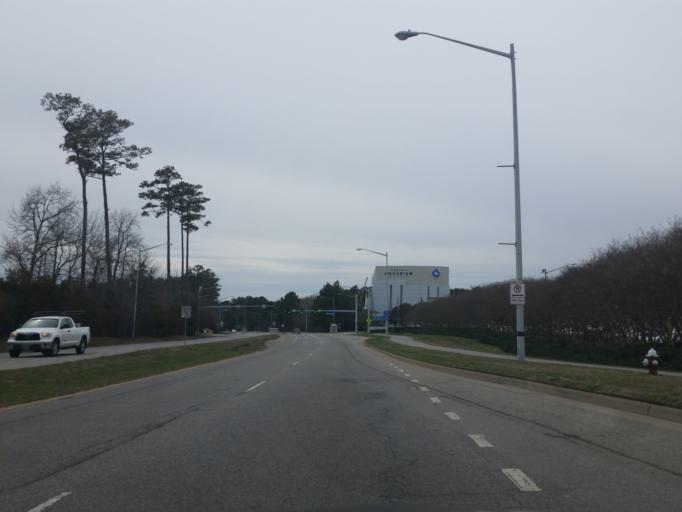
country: US
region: Virginia
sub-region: City of Virginia Beach
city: Virginia Beach
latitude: 36.8220
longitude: -75.9808
